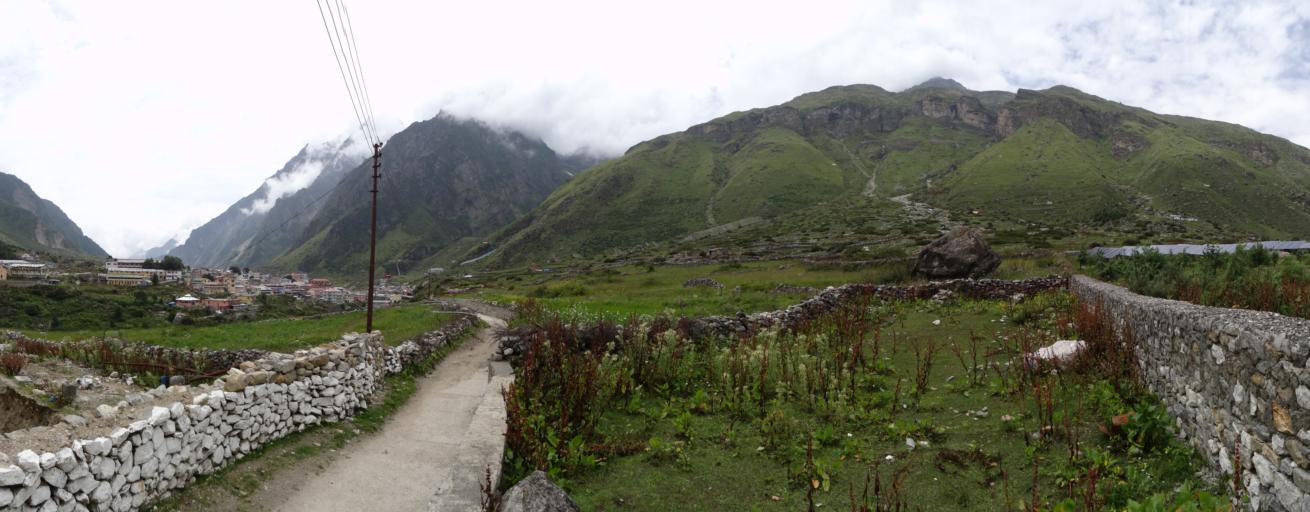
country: IN
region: Uttarakhand
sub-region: Chamoli
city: Joshimath
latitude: 30.7493
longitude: 79.4937
